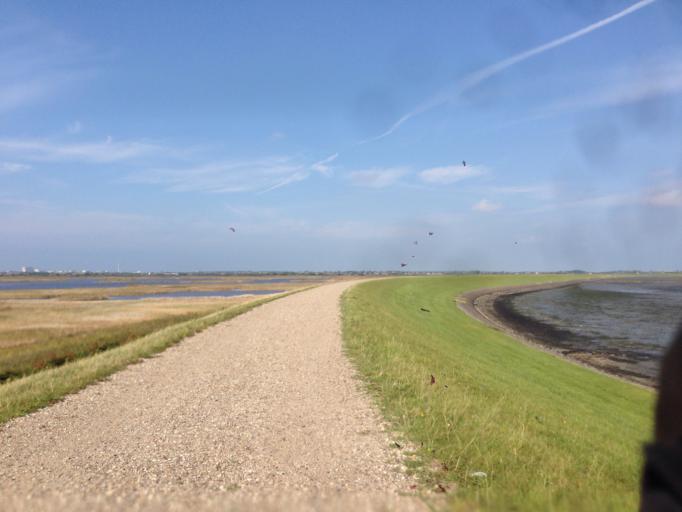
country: DE
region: Schleswig-Holstein
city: Tinnum
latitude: 54.8712
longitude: 8.3324
